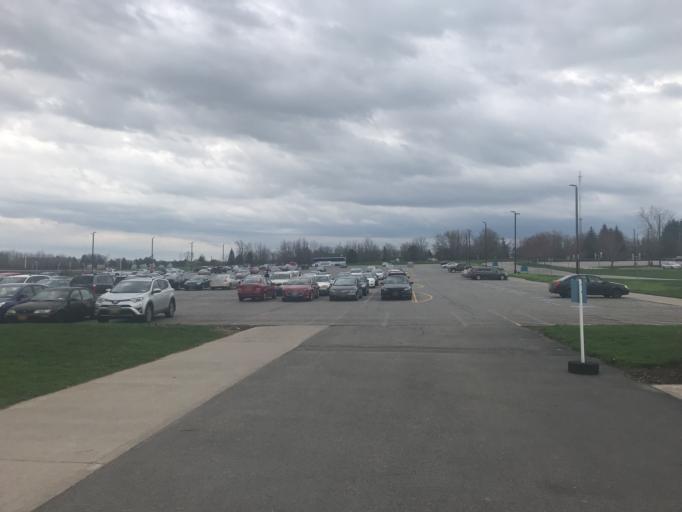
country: US
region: New York
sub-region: Monroe County
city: Rochester
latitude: 43.0991
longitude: -77.6102
